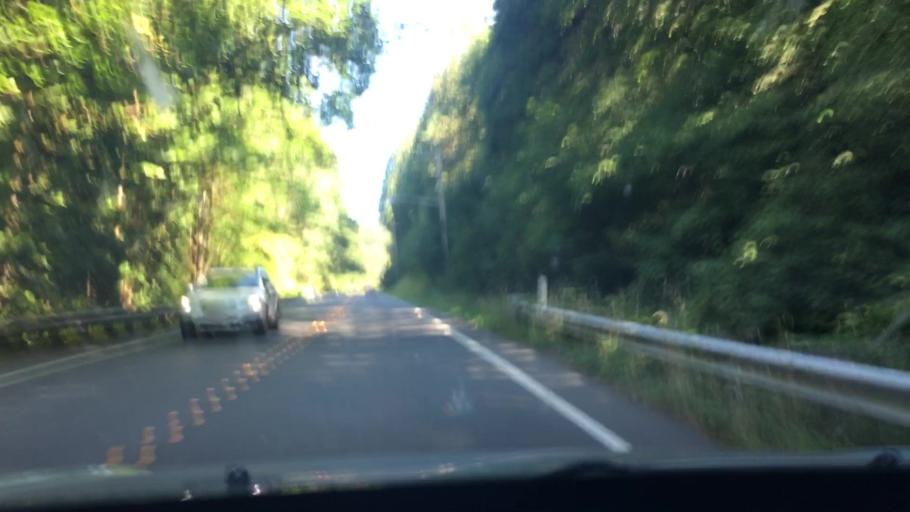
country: US
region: Washington
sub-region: King County
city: Newcastle
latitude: 47.5398
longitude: -122.1294
